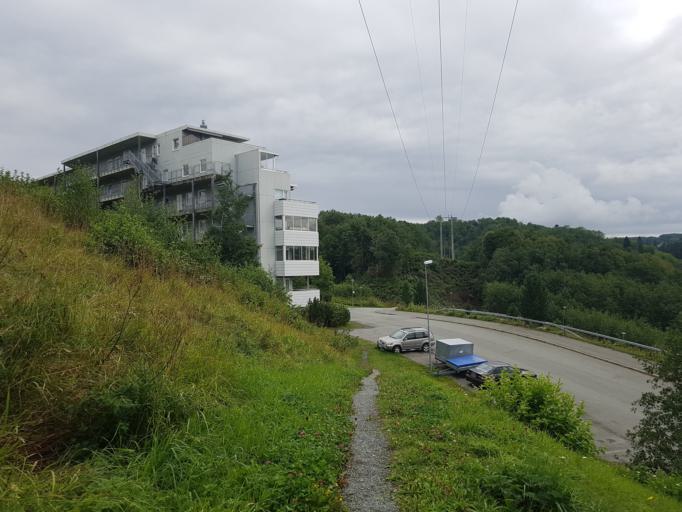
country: NO
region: Sor-Trondelag
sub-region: Trondheim
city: Trondheim
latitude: 63.3862
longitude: 10.3961
